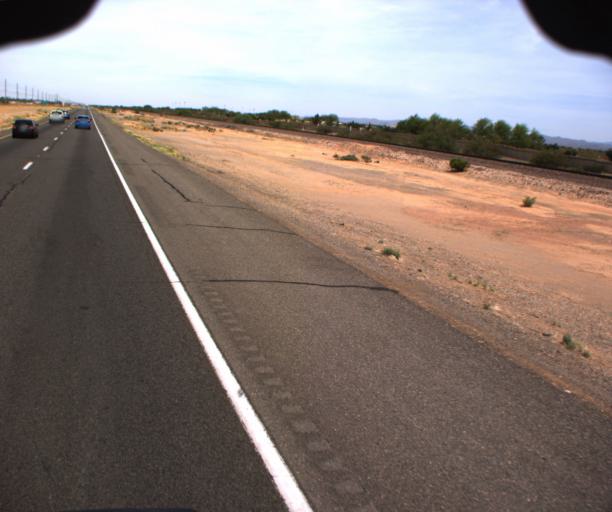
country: US
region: Arizona
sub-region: Maricopa County
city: Sun City West
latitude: 33.6876
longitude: -112.4128
